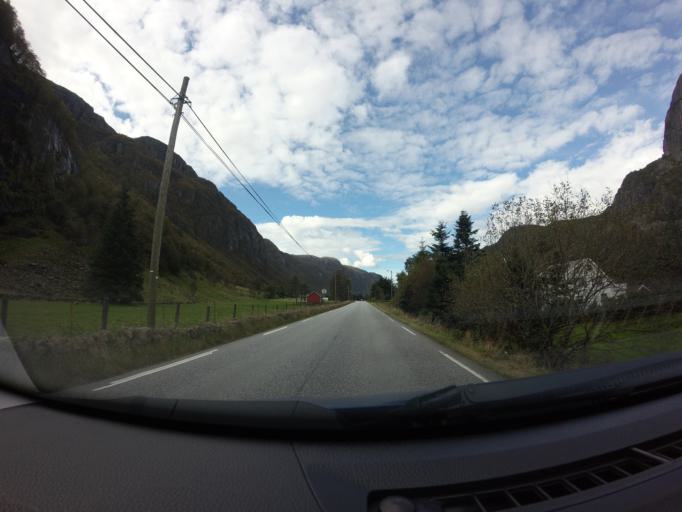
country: NO
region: Rogaland
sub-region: Forsand
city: Forsand
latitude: 58.8064
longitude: 6.2489
